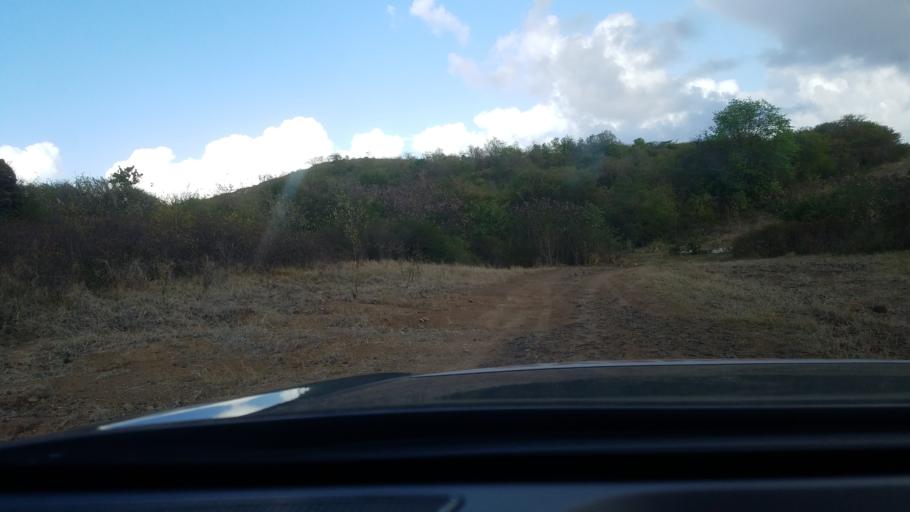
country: LC
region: Gros-Islet
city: Gros Islet
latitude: 14.0978
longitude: -60.9291
